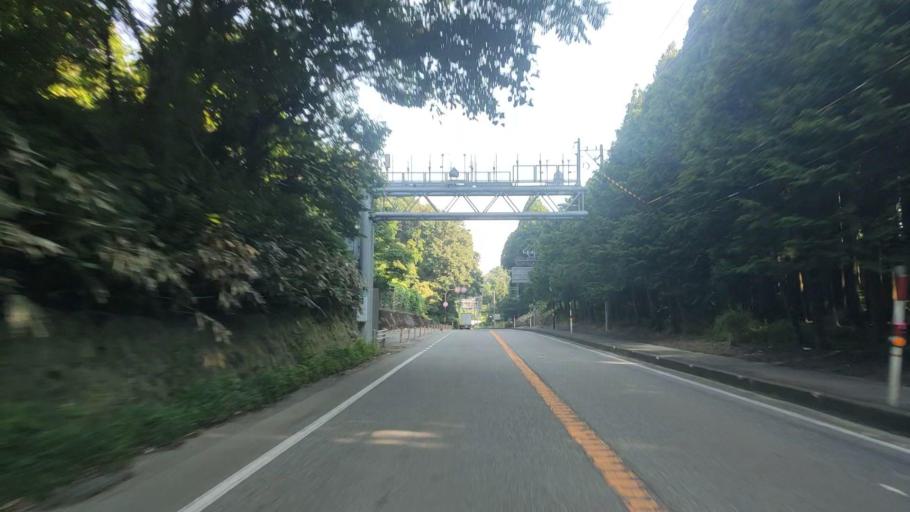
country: JP
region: Fukui
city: Maruoka
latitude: 36.2386
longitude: 136.2859
